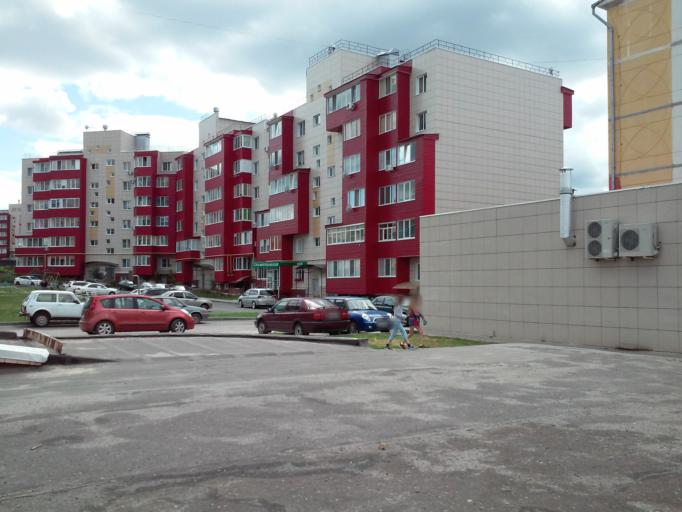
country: RU
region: Belgorod
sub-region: Belgorodskiy Rayon
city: Belgorod
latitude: 50.5369
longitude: 36.5769
